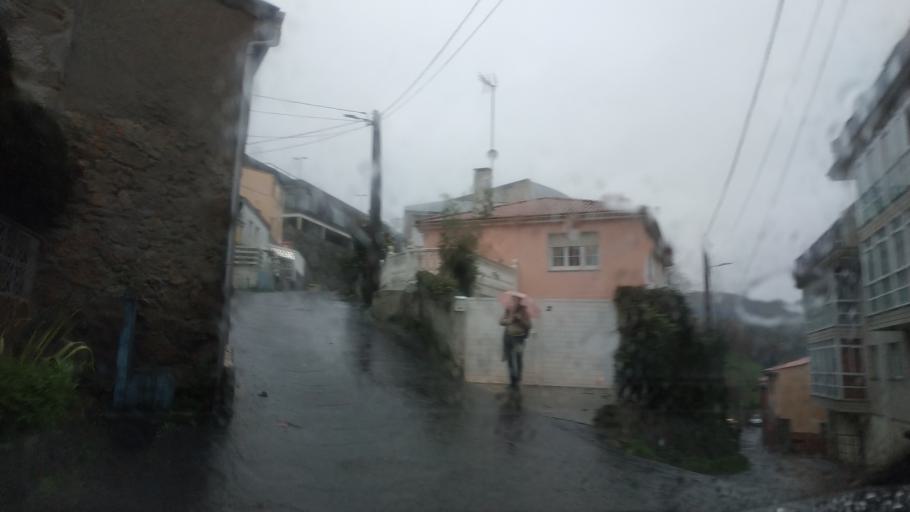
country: ES
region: Galicia
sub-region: Provincia da Coruna
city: A Coruna
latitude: 43.3292
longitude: -8.4086
